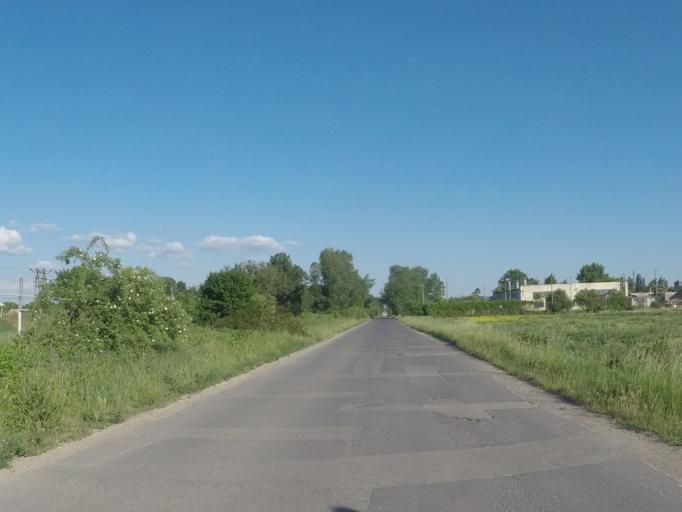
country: HU
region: Borsod-Abauj-Zemplen
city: Mucsony
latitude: 48.2466
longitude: 20.6662
